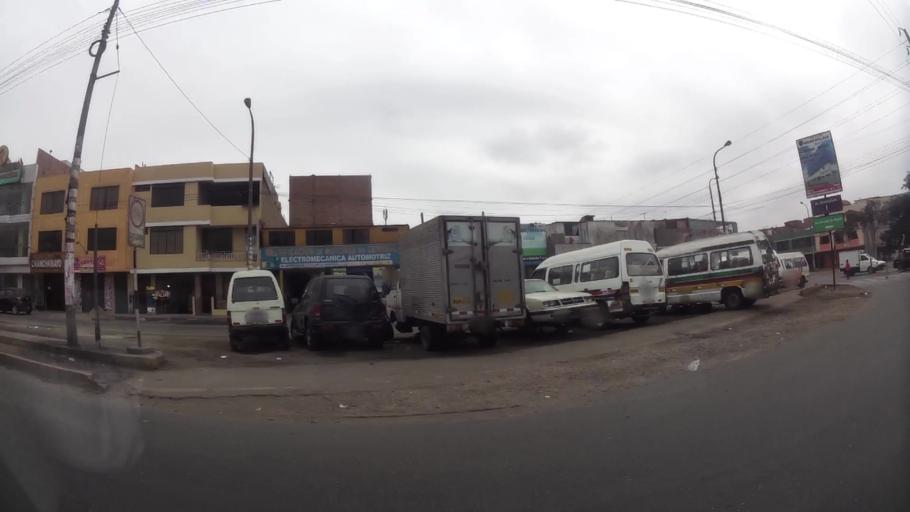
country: PE
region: Lima
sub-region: Lima
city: Independencia
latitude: -11.9970
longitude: -77.0851
